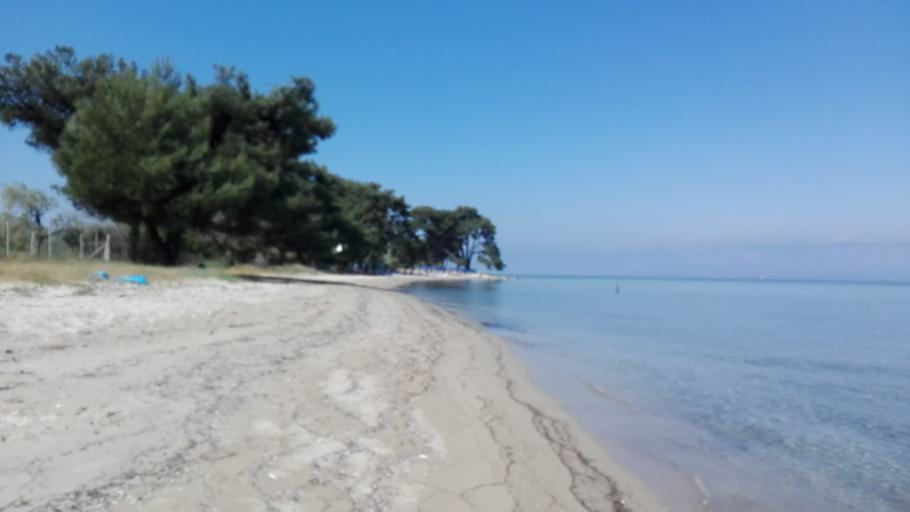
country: GR
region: East Macedonia and Thrace
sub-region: Nomos Kavalas
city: Prinos
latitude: 40.7791
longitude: 24.6071
